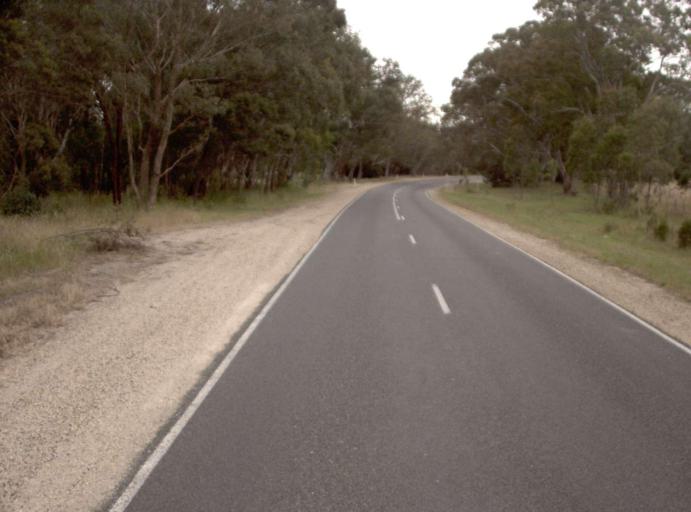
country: AU
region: Victoria
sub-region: Wellington
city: Sale
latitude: -38.1786
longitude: 147.1460
